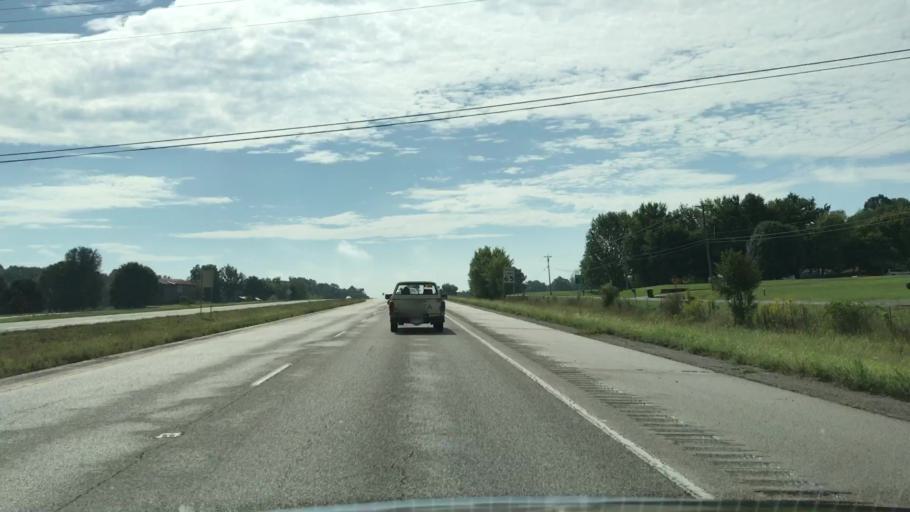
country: US
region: Kentucky
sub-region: Warren County
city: Plano
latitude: 36.8925
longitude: -86.3762
